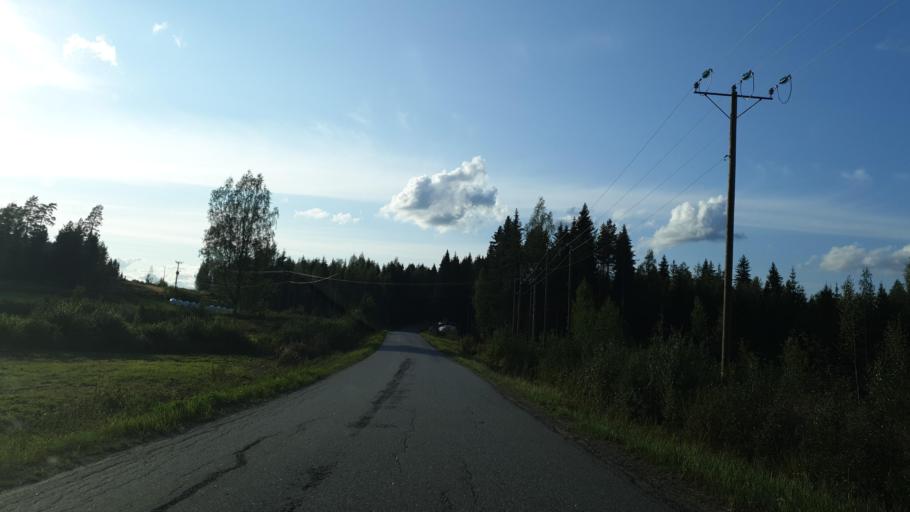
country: FI
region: Northern Savo
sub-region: Koillis-Savo
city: Kaavi
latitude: 63.0207
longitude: 28.6483
